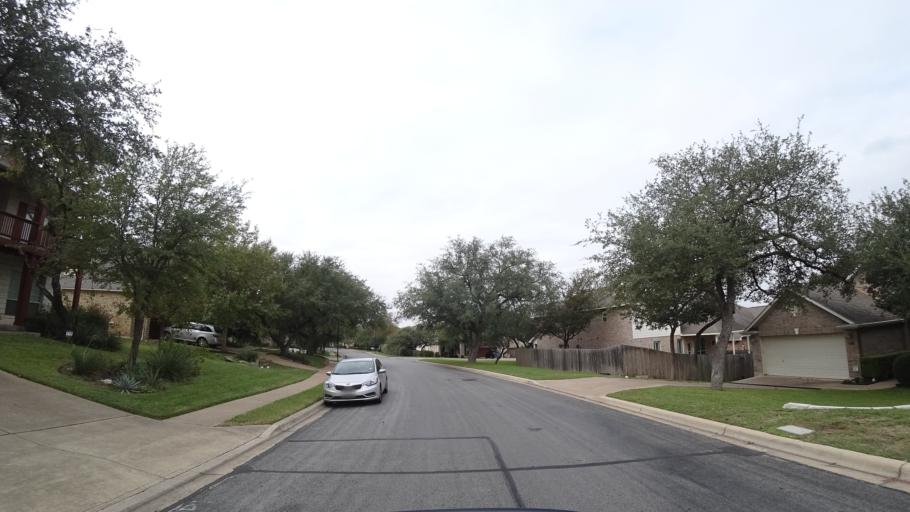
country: US
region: Texas
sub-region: Travis County
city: Shady Hollow
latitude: 30.1920
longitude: -97.8966
